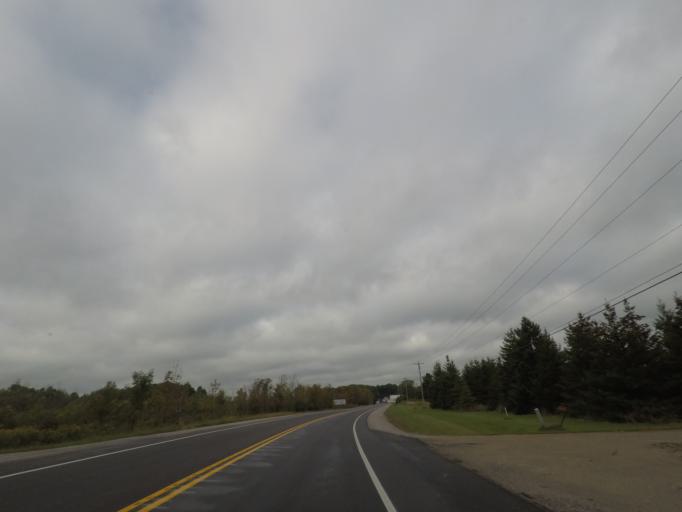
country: US
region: Wisconsin
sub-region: Jefferson County
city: Jefferson
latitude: 43.0124
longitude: -88.7540
